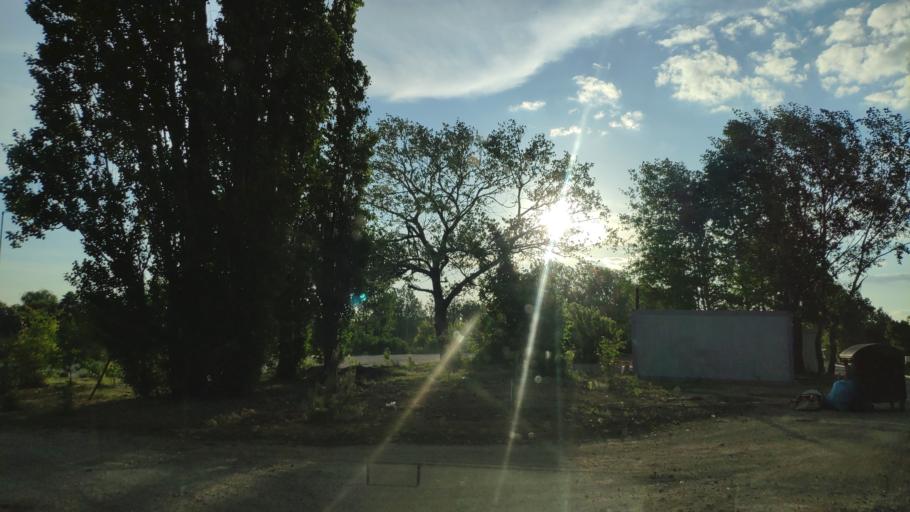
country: SK
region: Kosicky
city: Kosice
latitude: 48.6588
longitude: 21.3135
